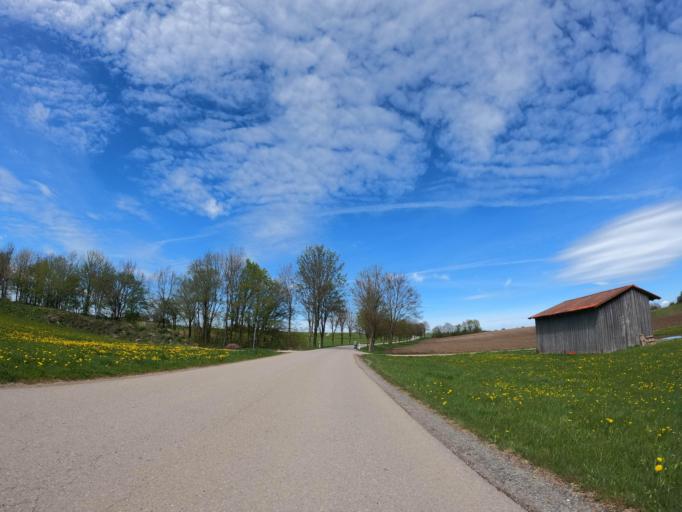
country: DE
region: Bavaria
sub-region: Upper Bavaria
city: Strasslach-Dingharting
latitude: 47.9730
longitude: 11.5167
